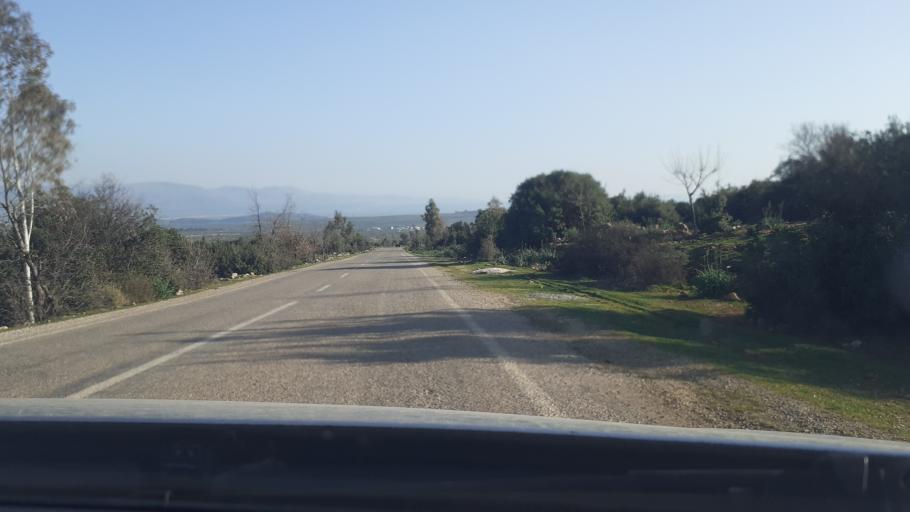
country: TR
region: Hatay
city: Aktepe
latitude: 36.7281
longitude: 36.4830
